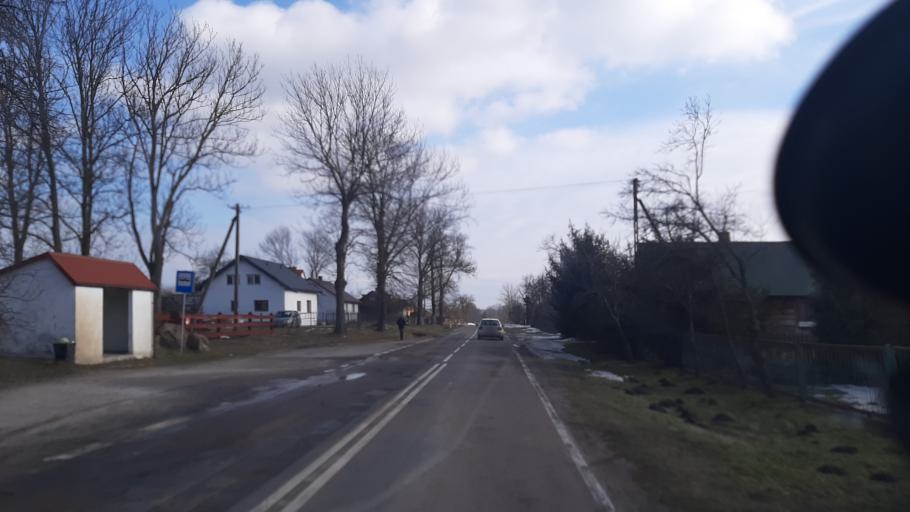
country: PL
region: Lublin Voivodeship
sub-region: Powiat parczewski
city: Sosnowica
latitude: 51.4993
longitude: 23.1592
